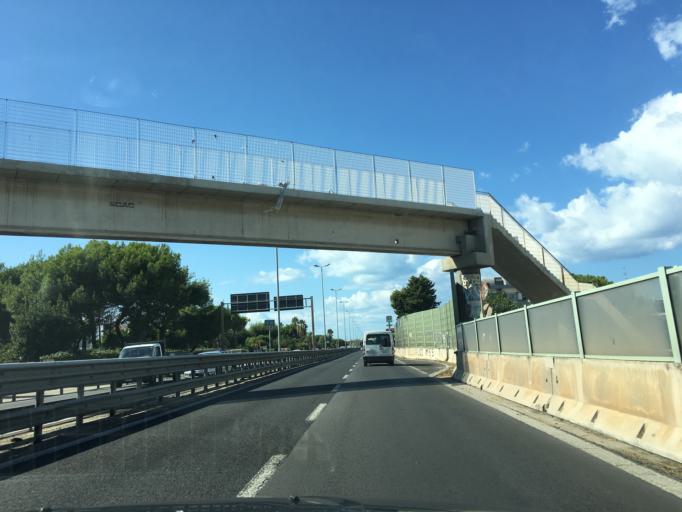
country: IT
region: Apulia
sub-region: Provincia di Bari
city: San Paolo
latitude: 41.1405
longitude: 16.8034
